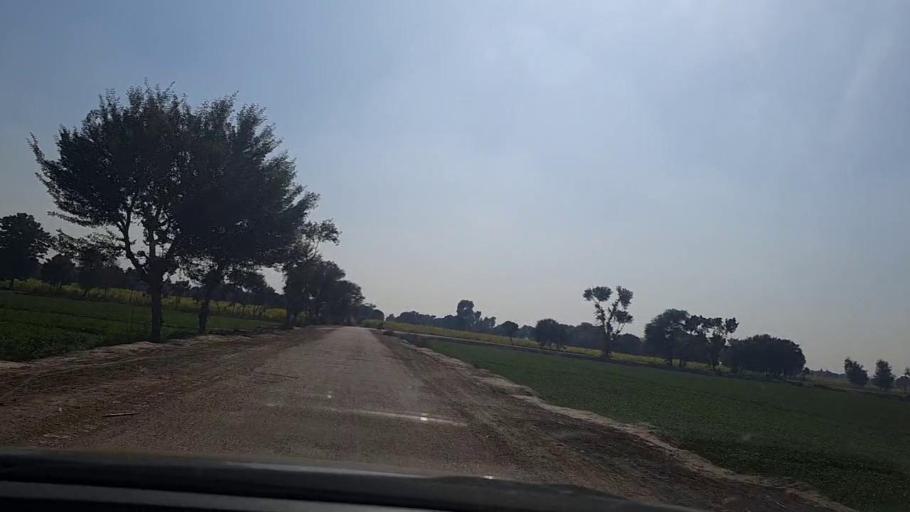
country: PK
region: Sindh
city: Daulatpur
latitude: 26.2860
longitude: 68.0678
